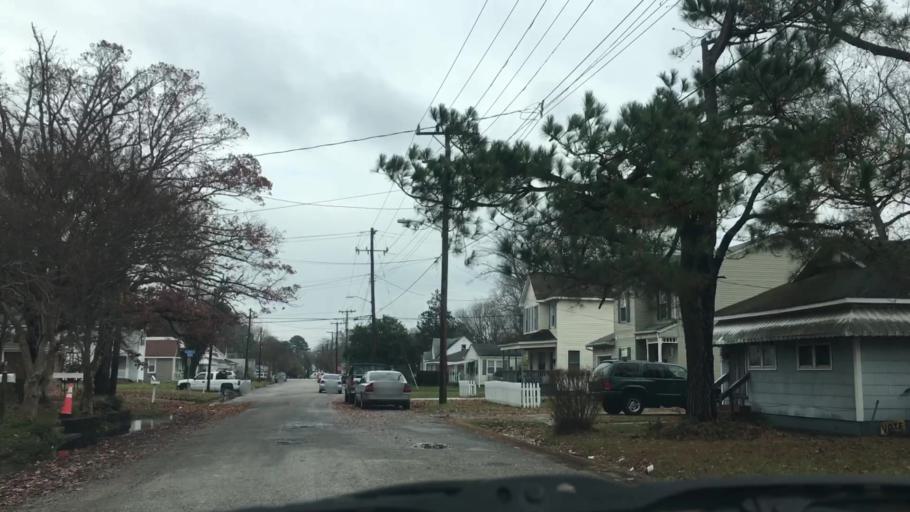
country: US
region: Virginia
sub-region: City of Norfolk
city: Norfolk
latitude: 36.8751
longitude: -76.2502
